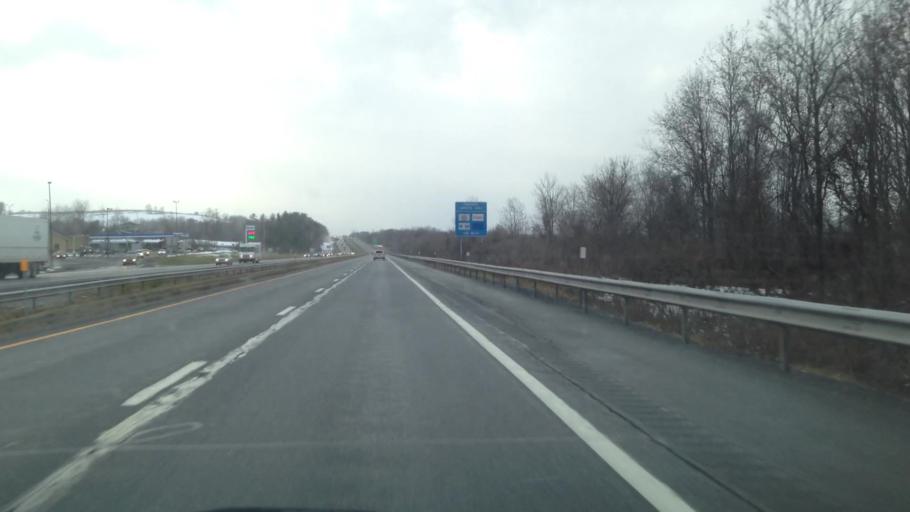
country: US
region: New York
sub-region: Montgomery County
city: Amsterdam
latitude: 42.9145
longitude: -74.1583
